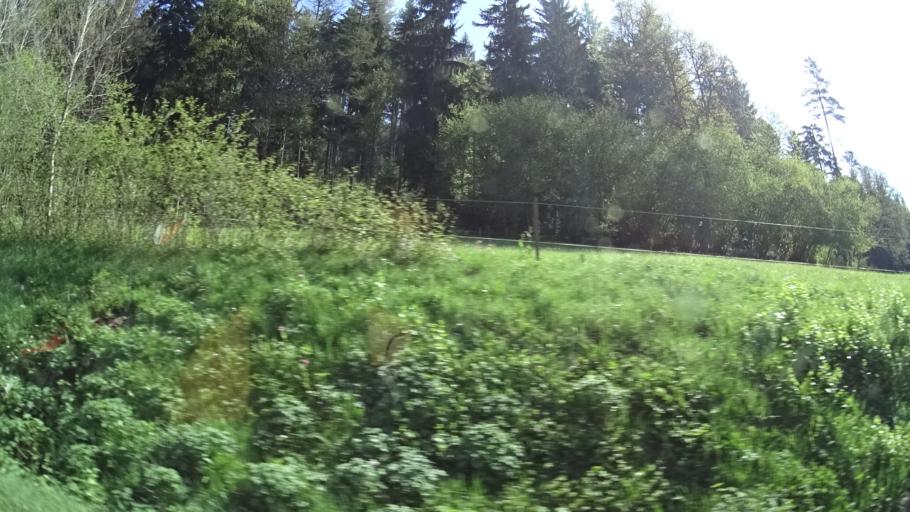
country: DE
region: Baden-Wuerttemberg
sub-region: Karlsruhe Region
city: Neuweiler
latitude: 48.6893
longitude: 8.5671
